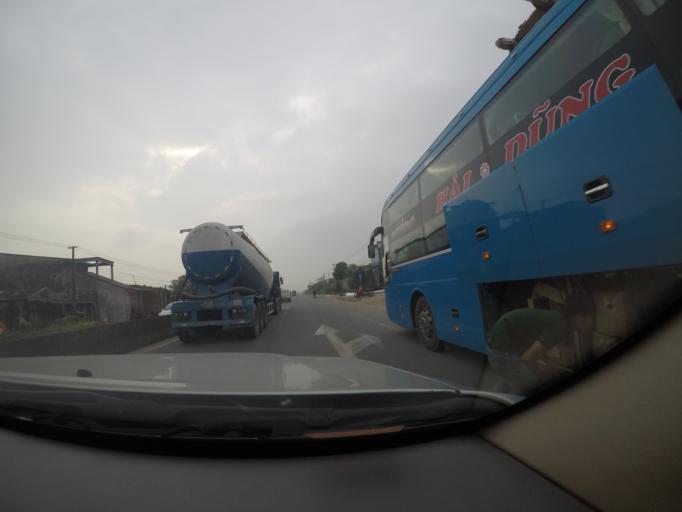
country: VN
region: Ha Tinh
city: Cam Xuyen
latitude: 18.1966
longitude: 106.1712
